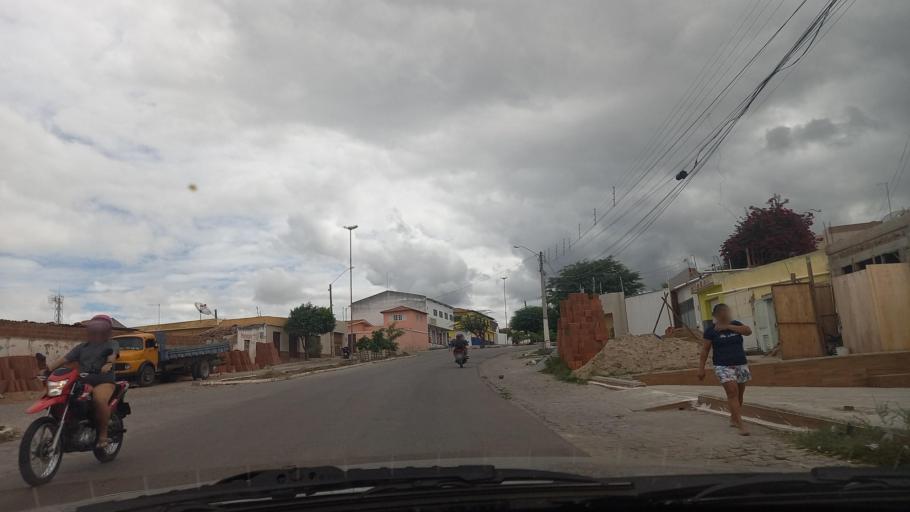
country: BR
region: Pernambuco
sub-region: Caruaru
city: Caruaru
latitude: -8.3259
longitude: -36.1390
